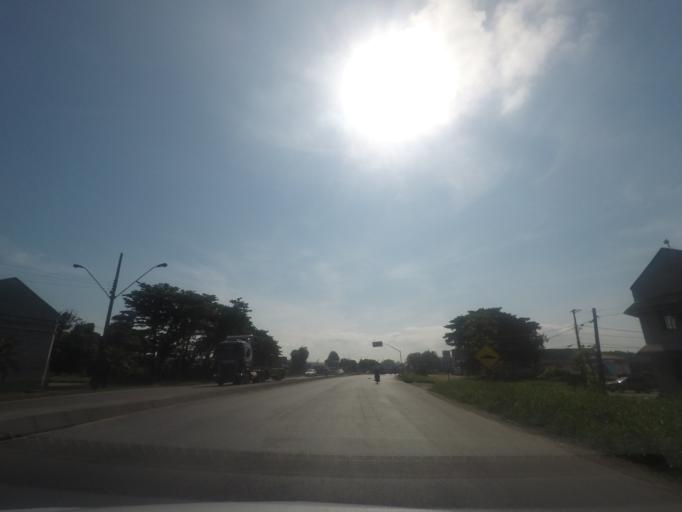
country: BR
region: Parana
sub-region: Paranagua
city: Paranagua
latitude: -25.5163
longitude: -48.5234
